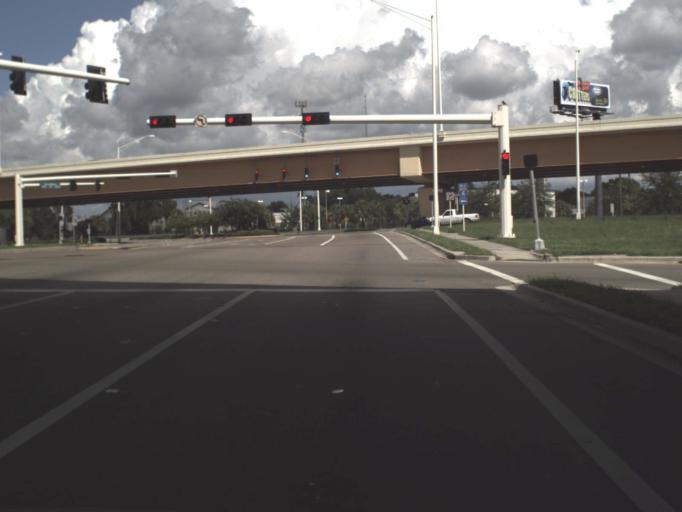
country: US
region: Florida
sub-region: Hillsborough County
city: East Lake-Orient Park
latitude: 27.9657
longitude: -82.4050
